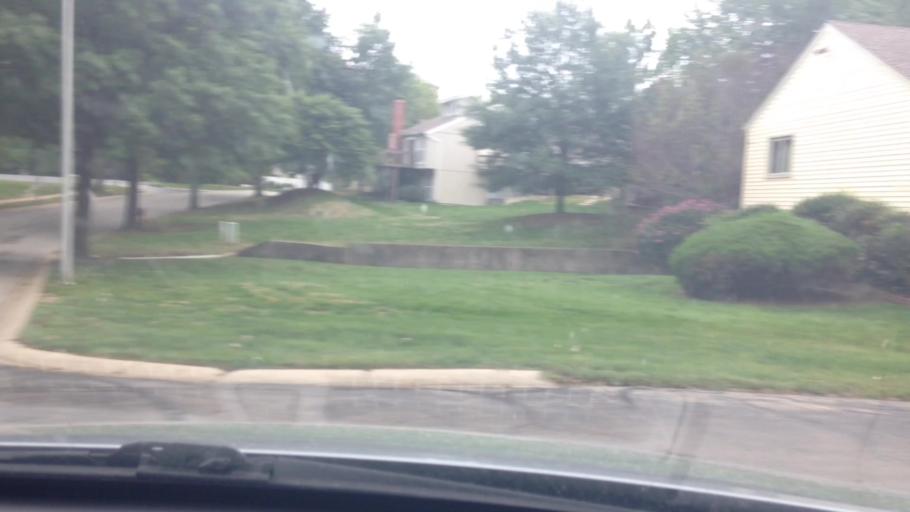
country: US
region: Missouri
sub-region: Platte County
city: Weatherby Lake
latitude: 39.2448
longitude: -94.6404
